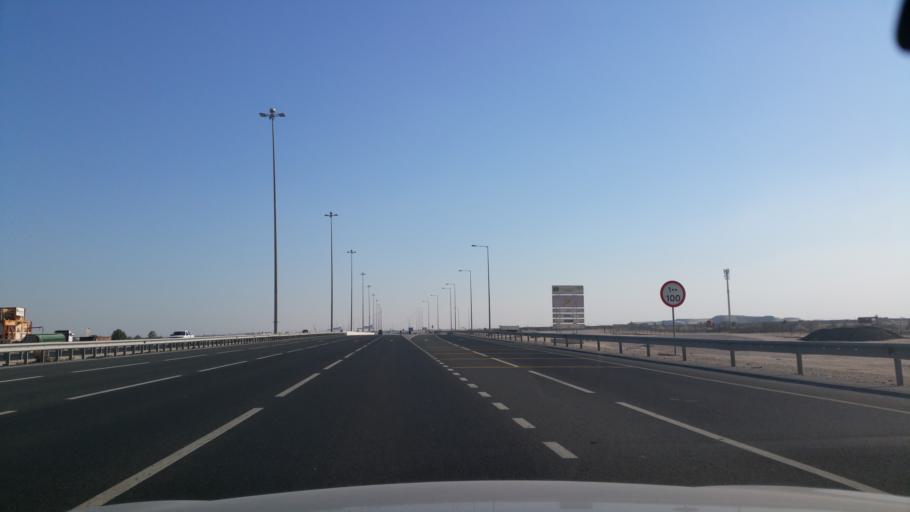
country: QA
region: Al Wakrah
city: Al Wukayr
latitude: 25.1540
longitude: 51.4733
